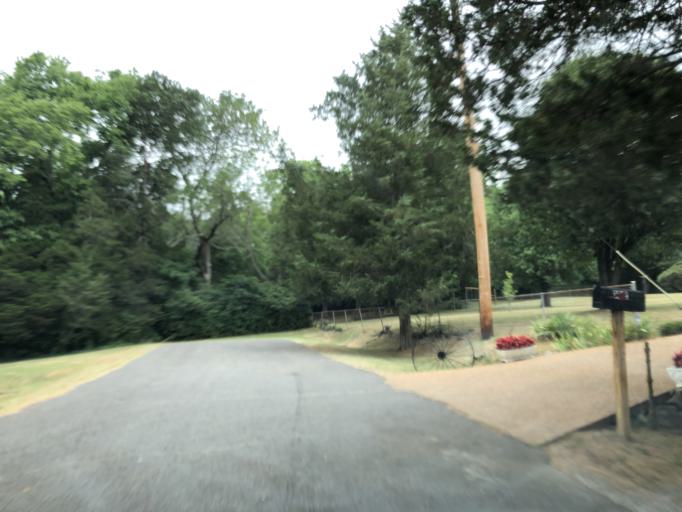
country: US
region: Tennessee
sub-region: Davidson County
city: Goodlettsville
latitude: 36.2905
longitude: -86.7315
